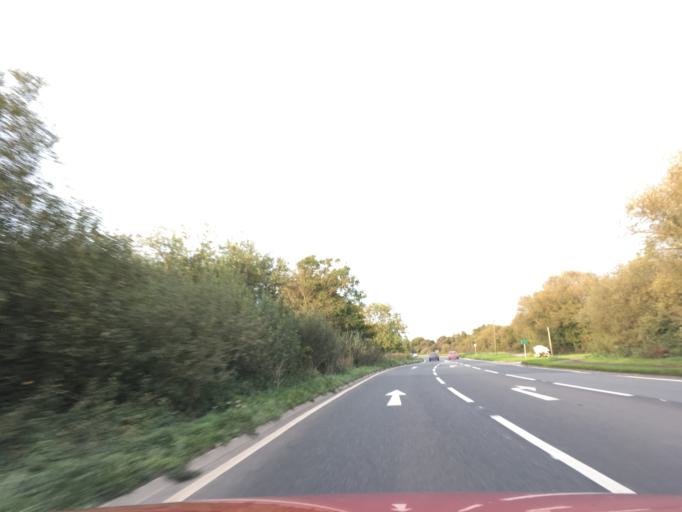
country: GB
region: England
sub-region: South Gloucestershire
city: Severn Beach
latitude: 51.5838
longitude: -2.6384
